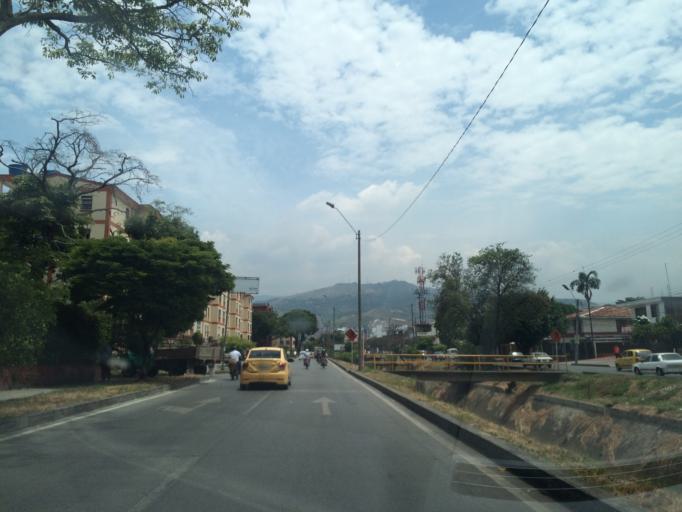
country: CO
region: Valle del Cauca
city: Cali
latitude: 3.4195
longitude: -76.5316
